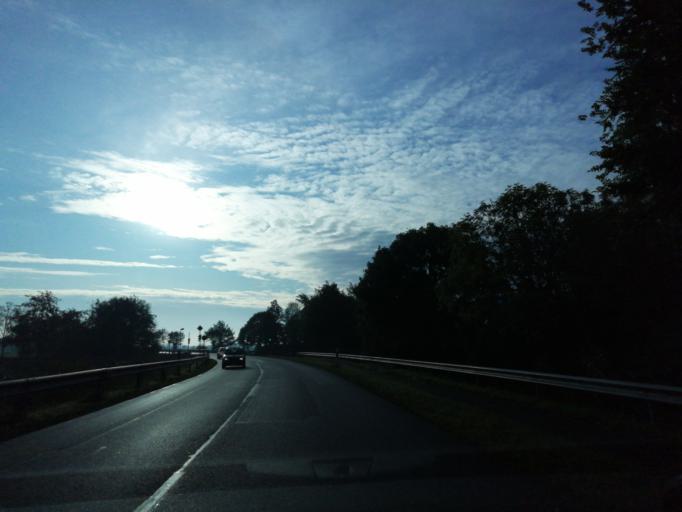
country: DE
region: Lower Saxony
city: Sillenstede
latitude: 53.6246
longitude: 8.0157
